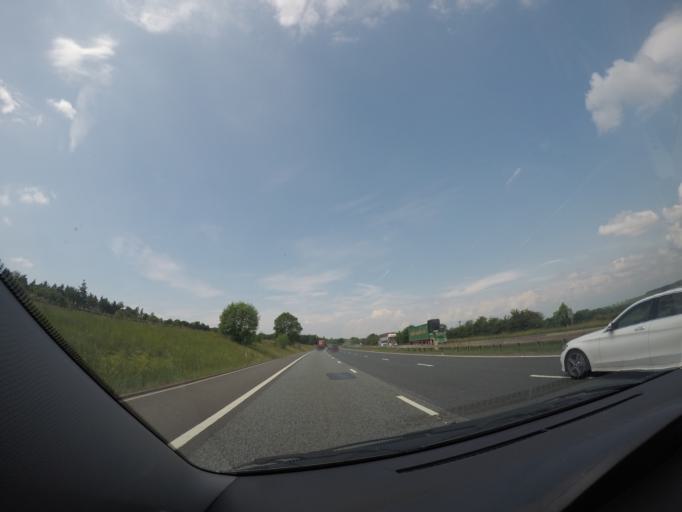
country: GB
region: England
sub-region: Cumbria
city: Scotby
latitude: 54.7898
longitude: -2.8652
